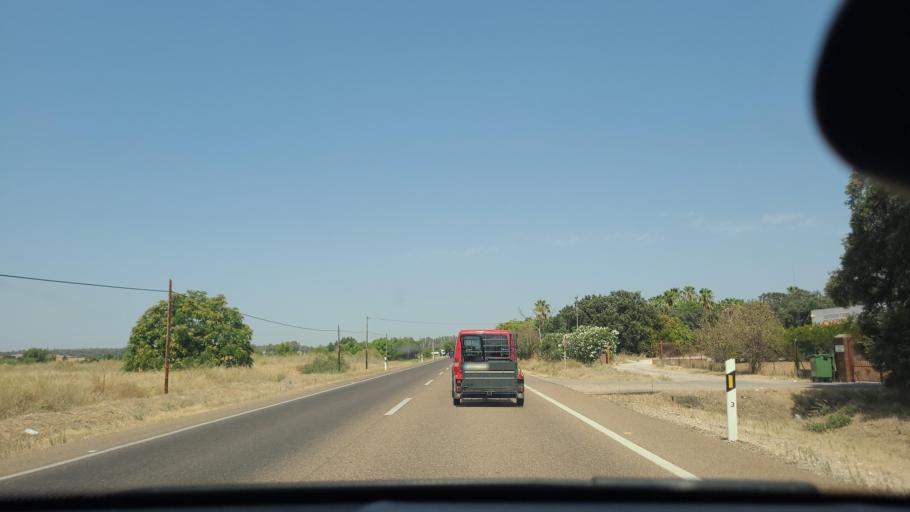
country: ES
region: Extremadura
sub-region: Provincia de Badajoz
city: Badajoz
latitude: 38.8295
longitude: -6.9165
